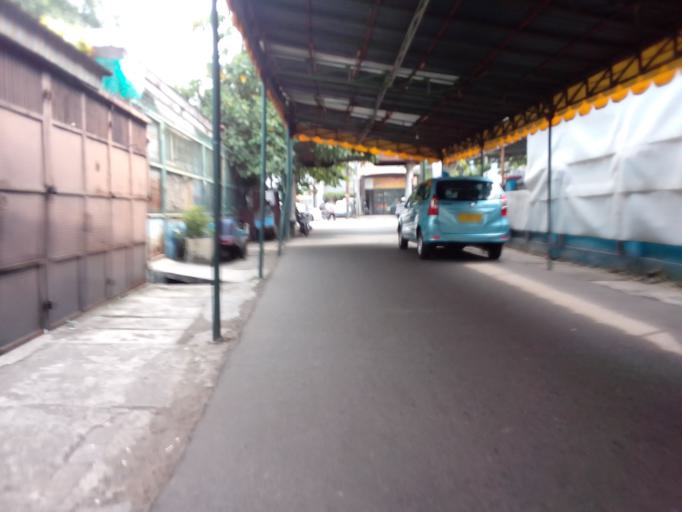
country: ID
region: Jakarta Raya
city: Jakarta
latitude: -6.1631
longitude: 106.8086
